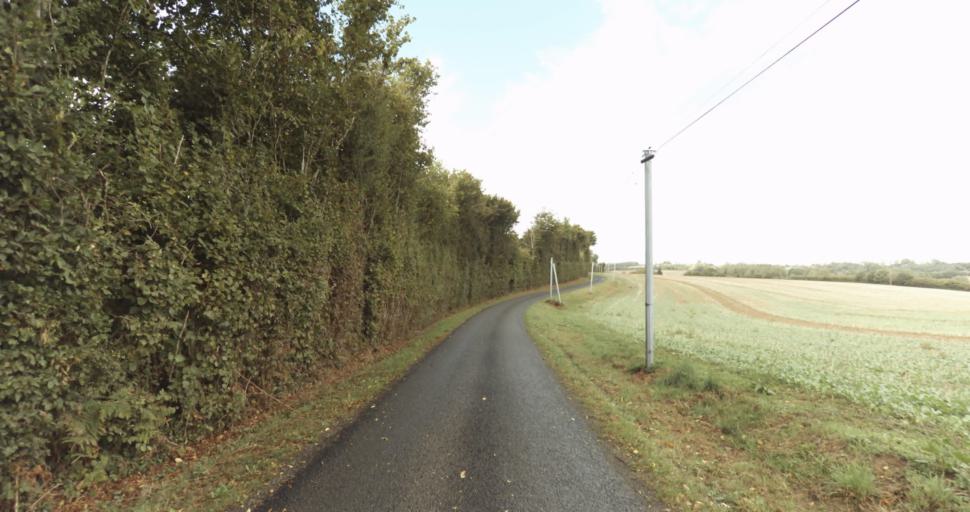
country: FR
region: Lower Normandy
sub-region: Departement de l'Orne
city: Sainte-Gauburge-Sainte-Colombe
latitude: 48.6865
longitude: 0.3754
